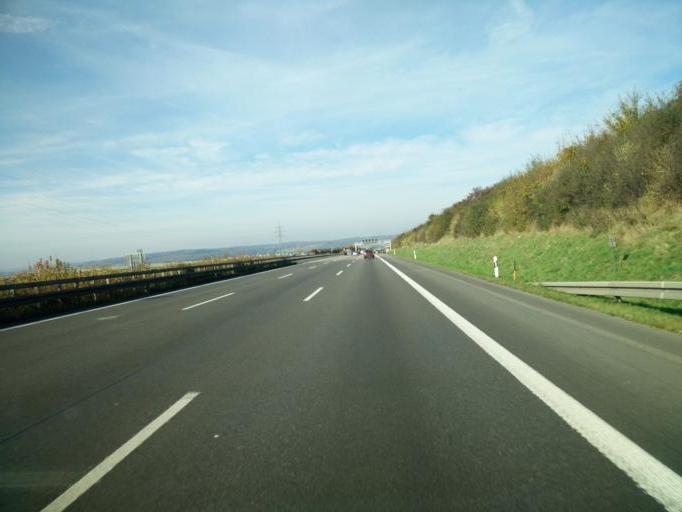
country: DE
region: Baden-Wuerttemberg
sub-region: Regierungsbezirk Stuttgart
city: Wendlingen am Neckar
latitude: 48.6541
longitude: 9.3930
